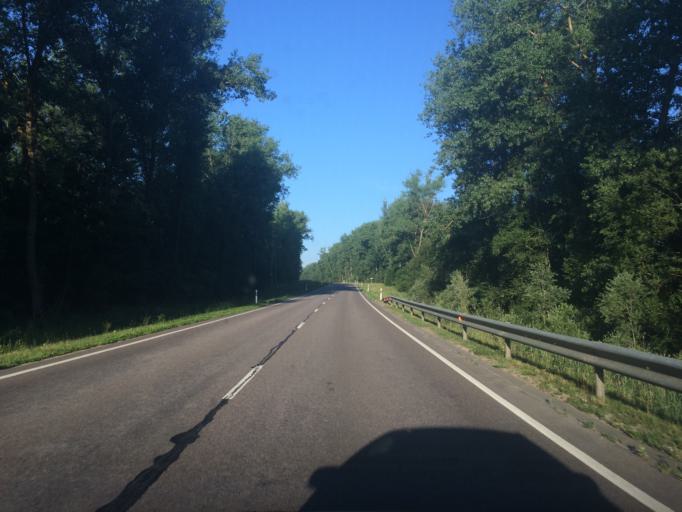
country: LT
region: Utenos apskritis
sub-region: Anyksciai
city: Anyksciai
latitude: 55.4306
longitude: 25.2435
